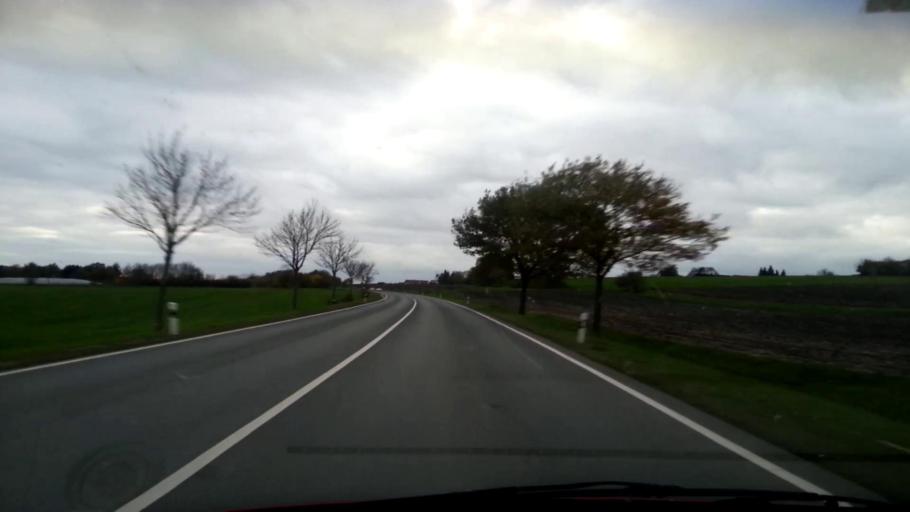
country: DE
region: Bavaria
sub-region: Upper Franconia
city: Kueps Oberfranken
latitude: 50.2127
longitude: 11.2687
